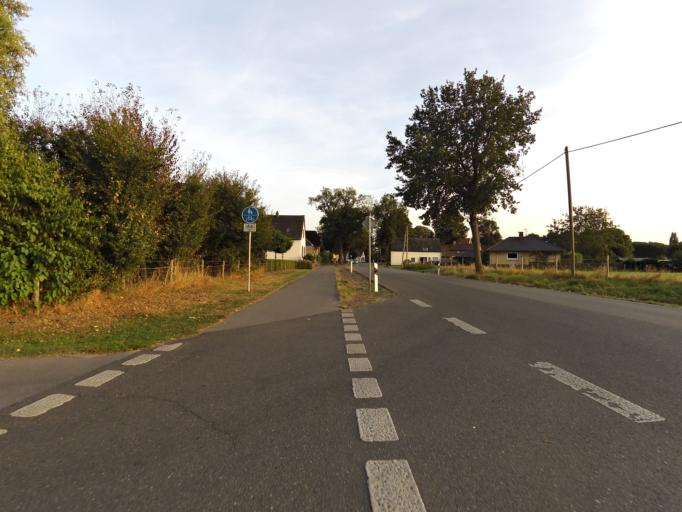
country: DE
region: North Rhine-Westphalia
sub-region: Regierungsbezirk Dusseldorf
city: Kleve
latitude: 51.8816
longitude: 6.1550
